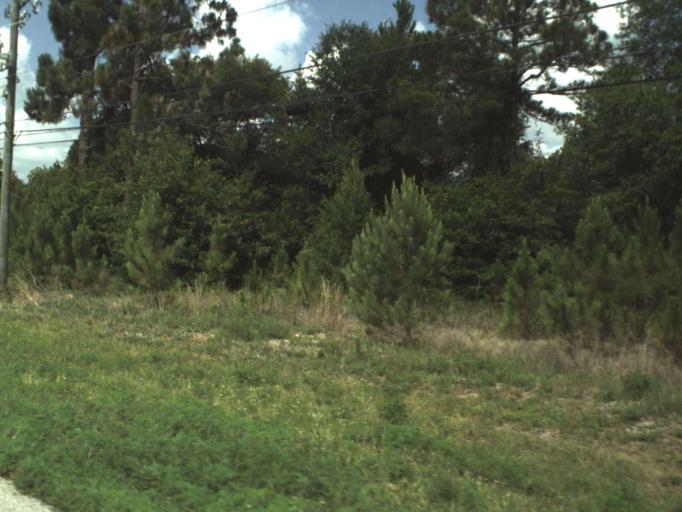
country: US
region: Florida
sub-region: Volusia County
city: Samsula-Spruce Creek
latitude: 28.9410
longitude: -81.1040
